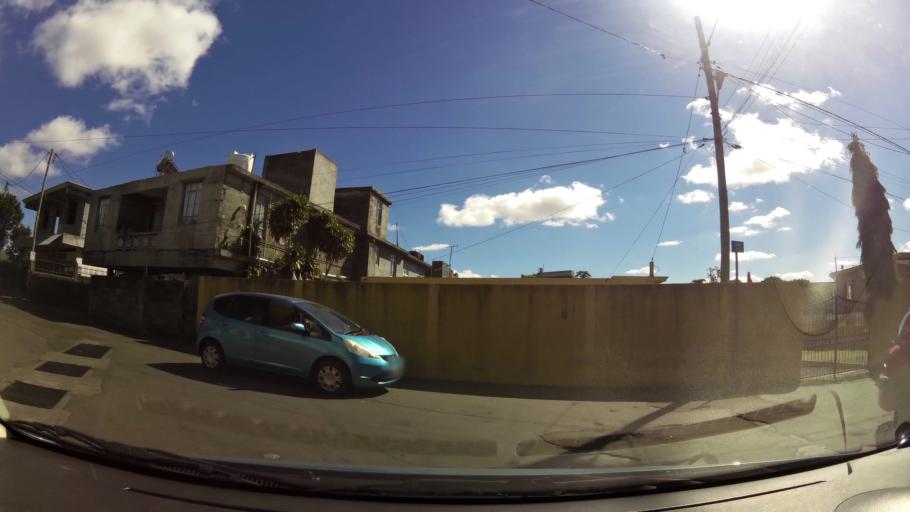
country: MU
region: Plaines Wilhems
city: Vacoas
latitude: -20.2911
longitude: 57.4778
